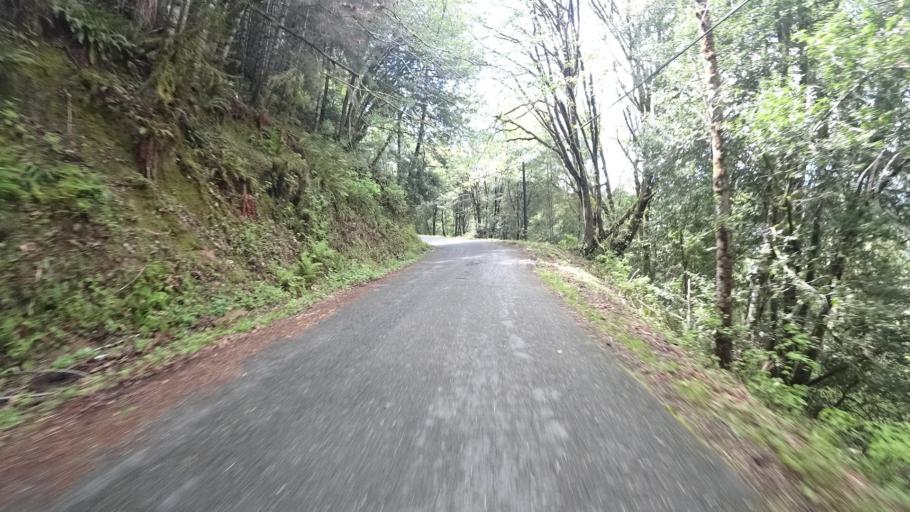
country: US
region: California
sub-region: Humboldt County
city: Blue Lake
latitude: 40.7621
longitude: -123.9016
